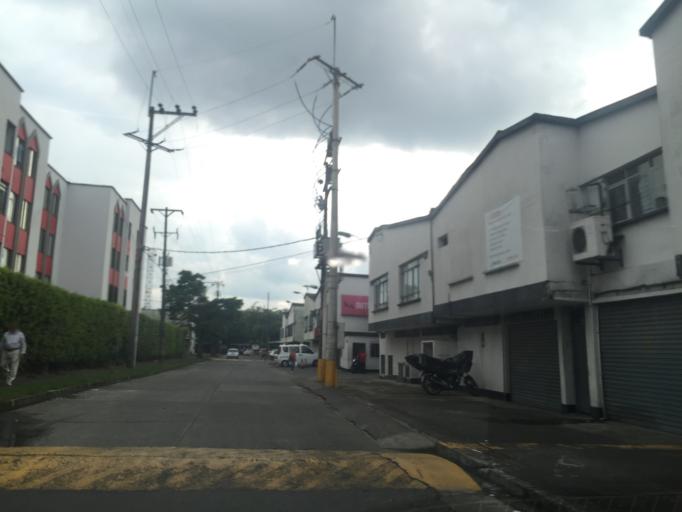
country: CO
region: Risaralda
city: Dos Quebradas
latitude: 4.8315
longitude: -75.6784
